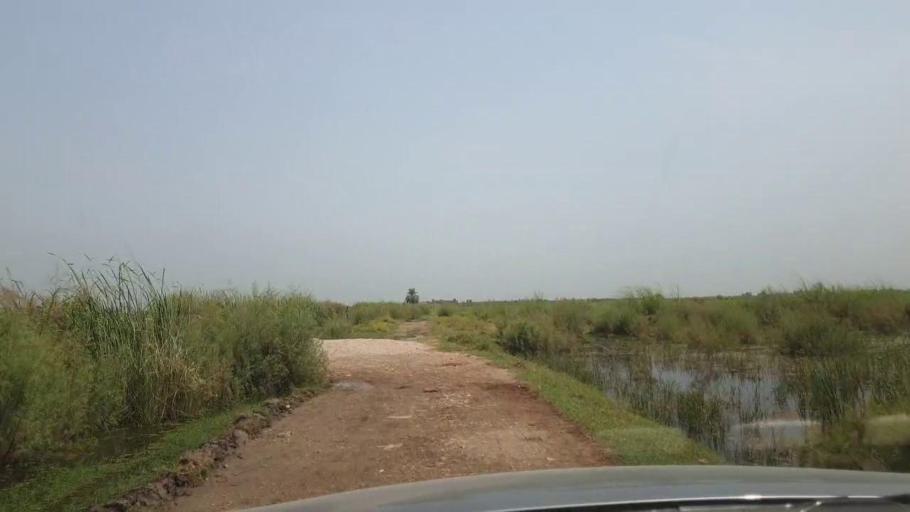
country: PK
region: Sindh
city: Madeji
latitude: 27.8145
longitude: 68.5093
